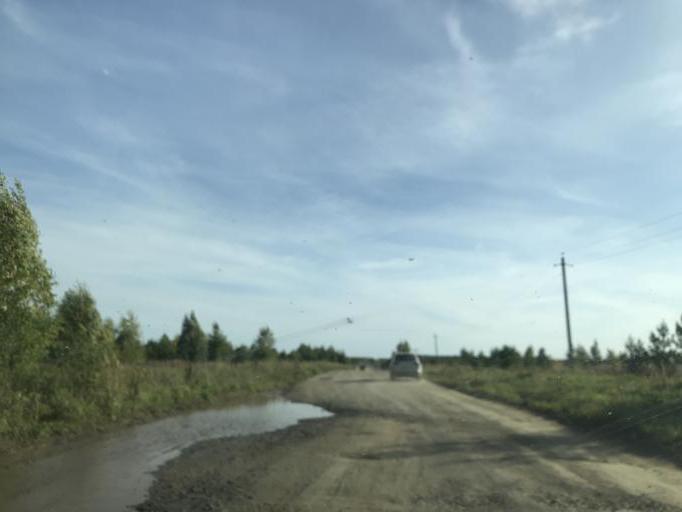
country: RU
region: Chelyabinsk
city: Poletayevo
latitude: 54.9753
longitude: 60.9701
